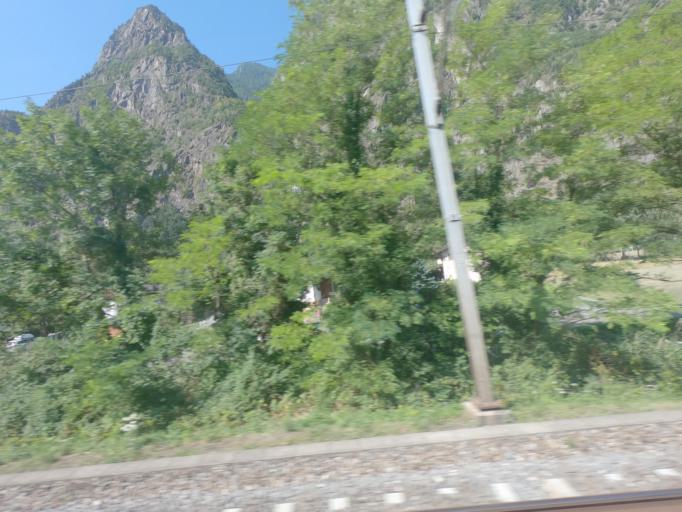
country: CH
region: Valais
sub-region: Saint-Maurice District
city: Vernayaz
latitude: 46.1457
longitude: 7.0320
